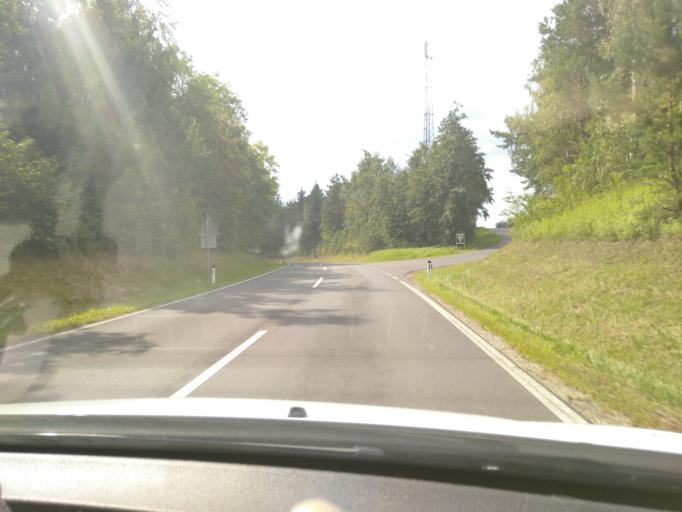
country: AT
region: Burgenland
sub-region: Politischer Bezirk Oberwart
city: Riedlingsdorf
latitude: 47.3629
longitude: 16.1400
